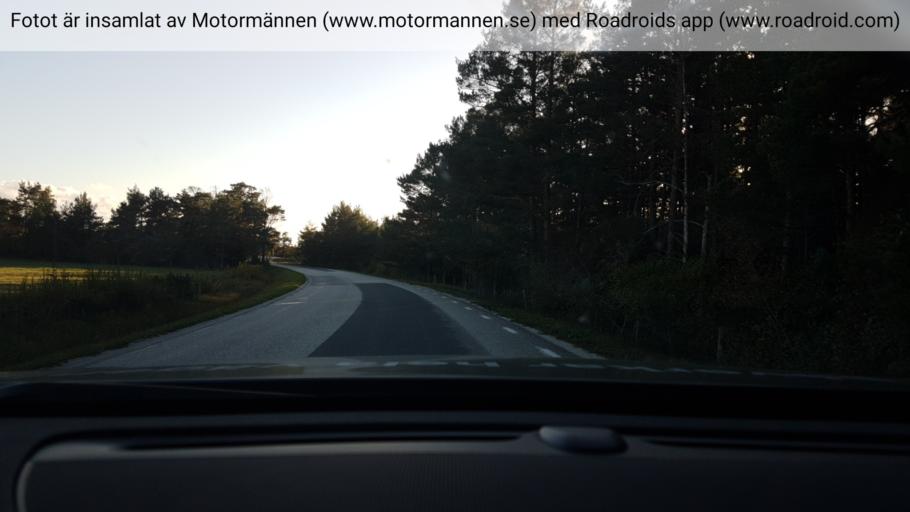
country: SE
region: Gotland
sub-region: Gotland
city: Slite
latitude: 57.8468
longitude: 18.6470
